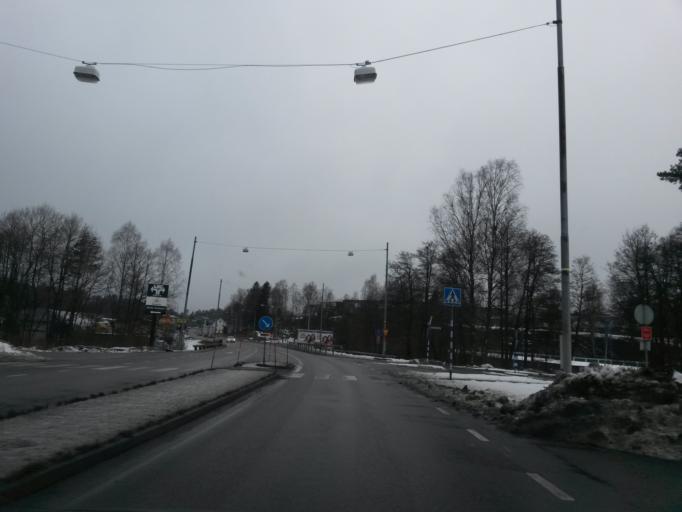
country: SE
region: Vaestra Goetaland
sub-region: Boras Kommun
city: Ganghester
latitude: 57.7036
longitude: 12.9786
